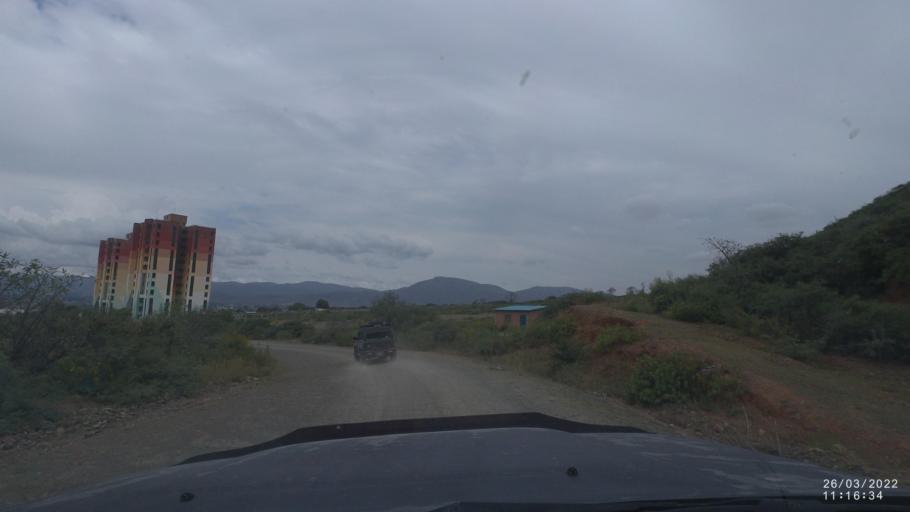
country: BO
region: Cochabamba
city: Tarata
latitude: -17.5352
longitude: -66.0232
